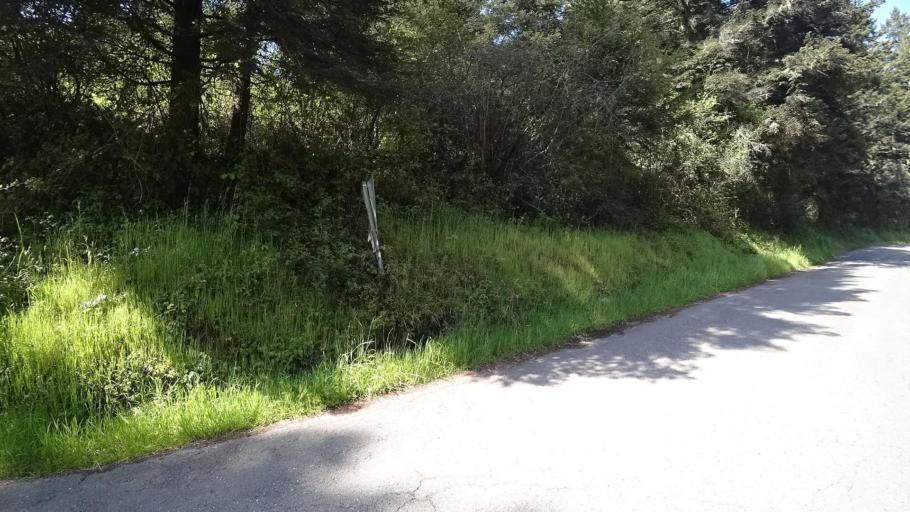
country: US
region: California
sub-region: Humboldt County
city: Hydesville
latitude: 40.5701
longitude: -124.1093
